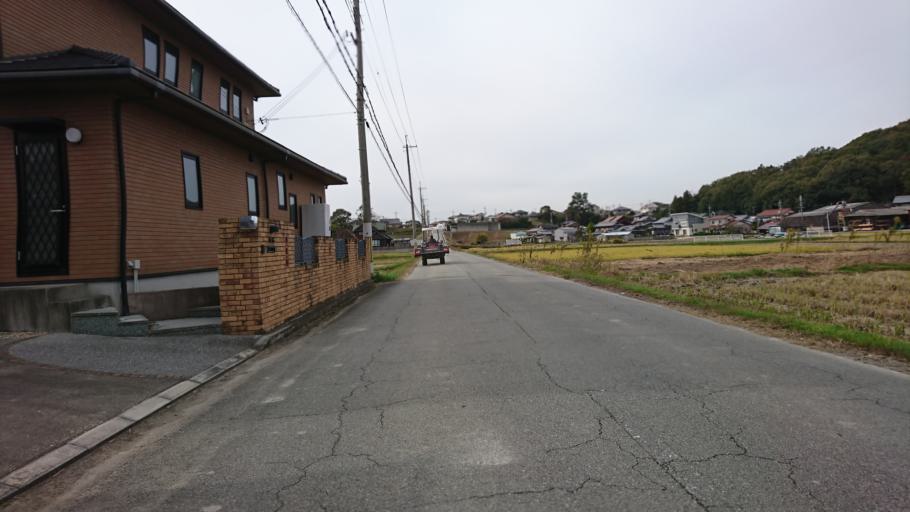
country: JP
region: Hyogo
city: Kakogawacho-honmachi
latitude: 34.7872
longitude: 134.8900
